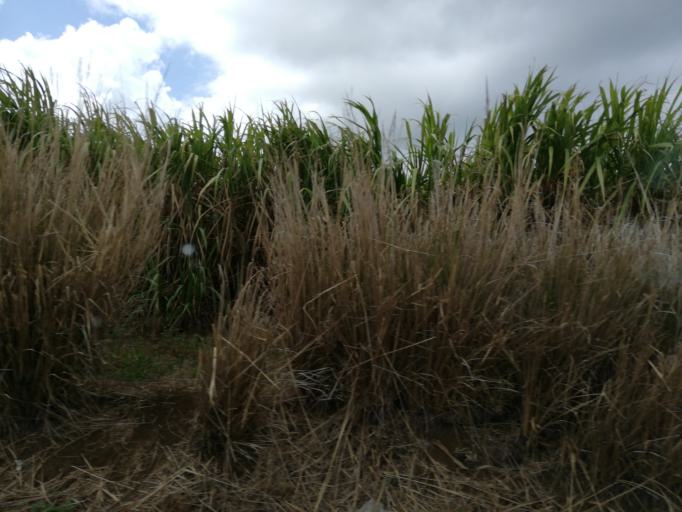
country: MU
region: Pamplemousses
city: Arsenal
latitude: -20.0926
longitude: 57.5431
